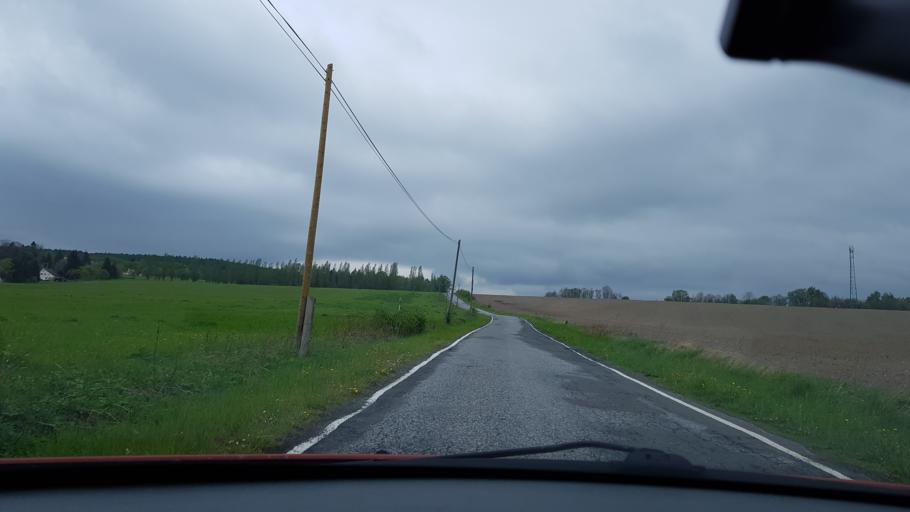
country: PL
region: Lower Silesian Voivodeship
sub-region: Powiat zabkowicki
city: Zloty Stok
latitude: 50.4434
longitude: 16.9059
